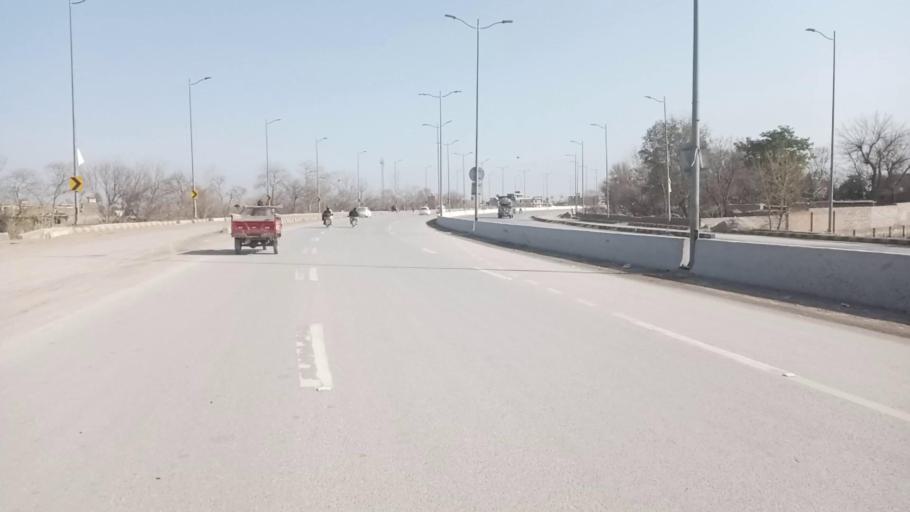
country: PK
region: Khyber Pakhtunkhwa
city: Peshawar
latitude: 34.0397
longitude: 71.5376
